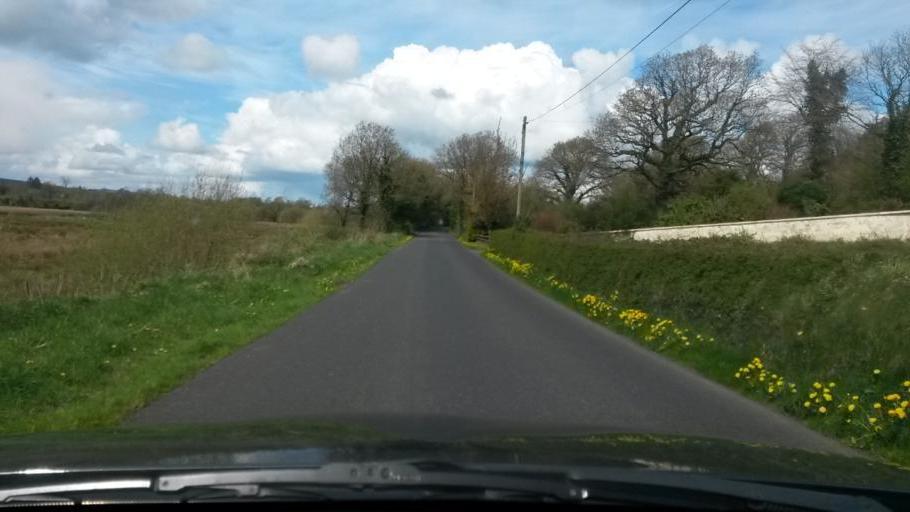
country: GB
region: Northern Ireland
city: Lisnaskea
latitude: 54.1863
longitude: -7.5050
